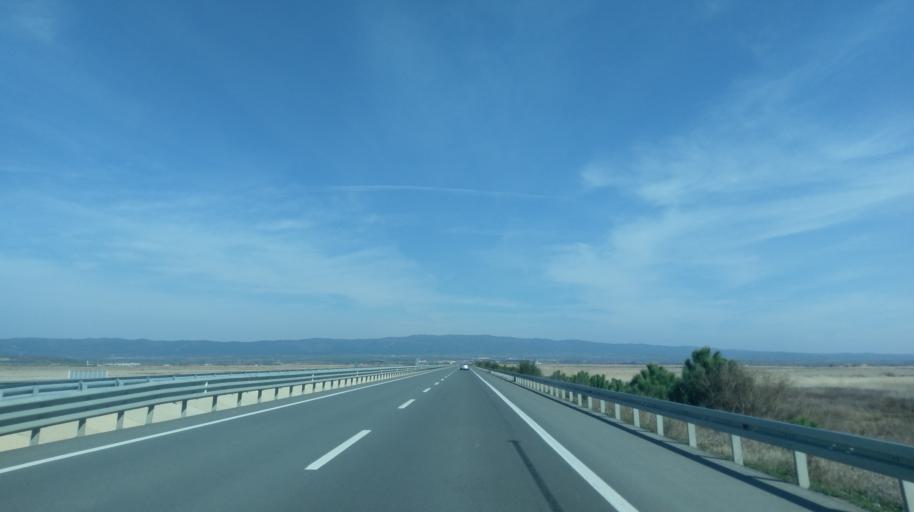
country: TR
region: Canakkale
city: Evrese
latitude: 40.6204
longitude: 26.8673
